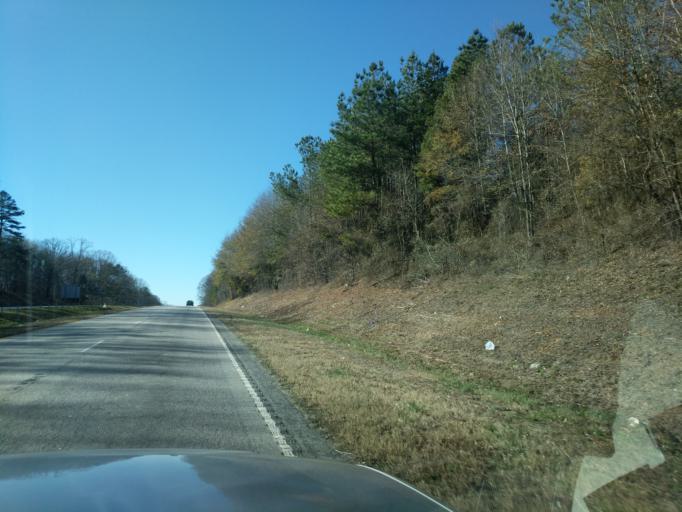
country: US
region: South Carolina
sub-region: Pickens County
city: Central
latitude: 34.7019
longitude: -82.7652
